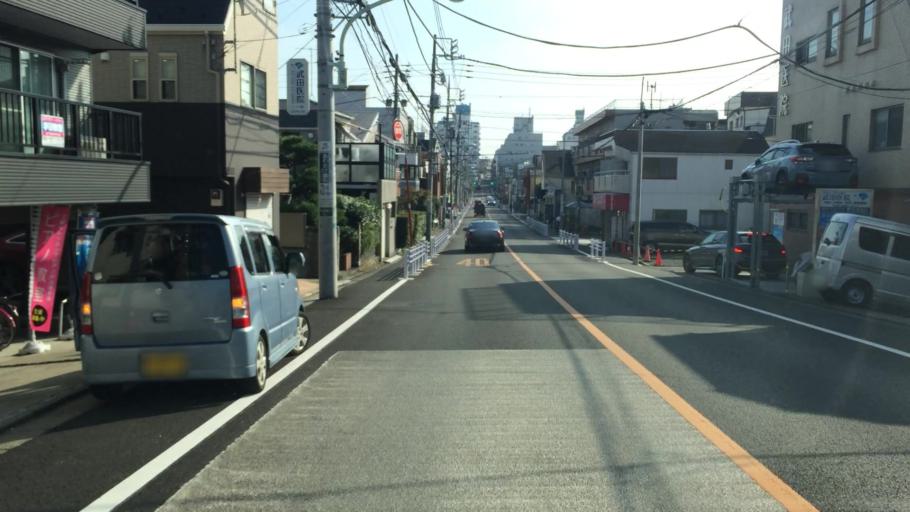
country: JP
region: Tokyo
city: Tokyo
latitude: 35.6188
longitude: 139.6680
